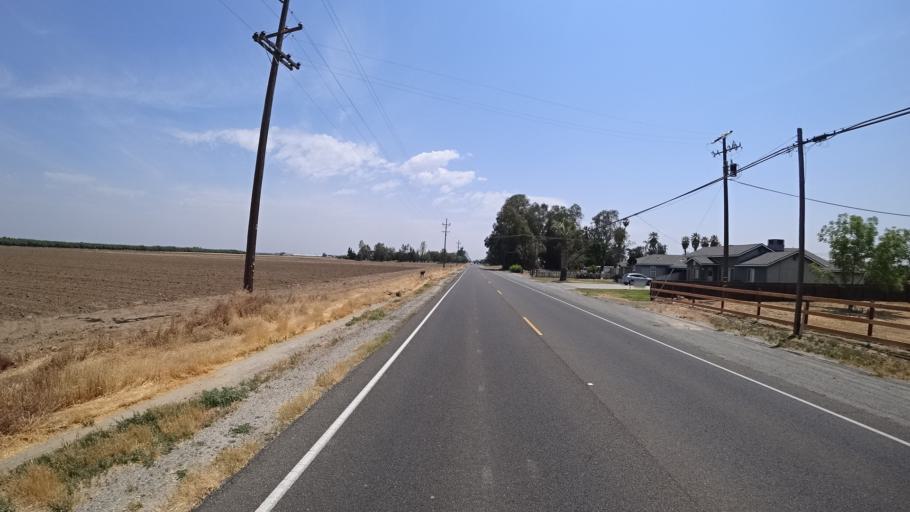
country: US
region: California
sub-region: Kings County
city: Armona
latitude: 36.3135
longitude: -119.7427
